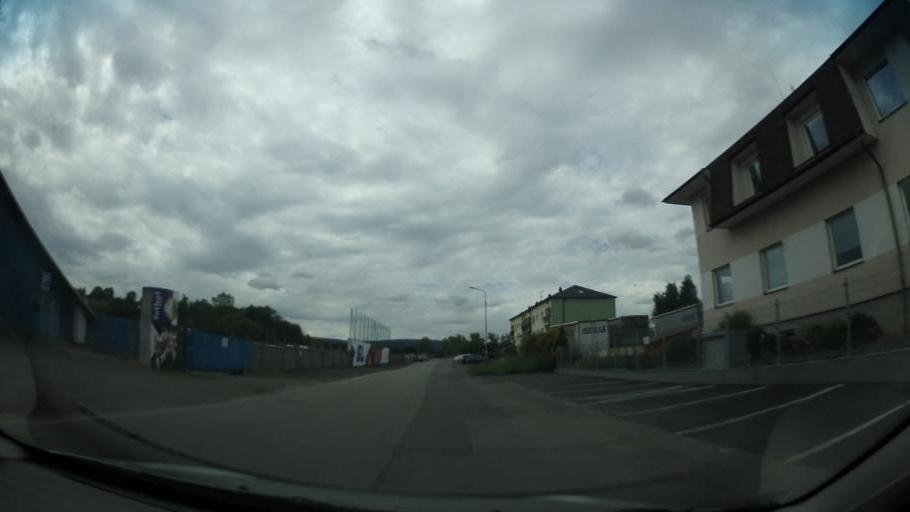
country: CZ
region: Pardubicky
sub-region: Okres Svitavy
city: Moravska Trebova
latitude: 49.7670
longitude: 16.6606
